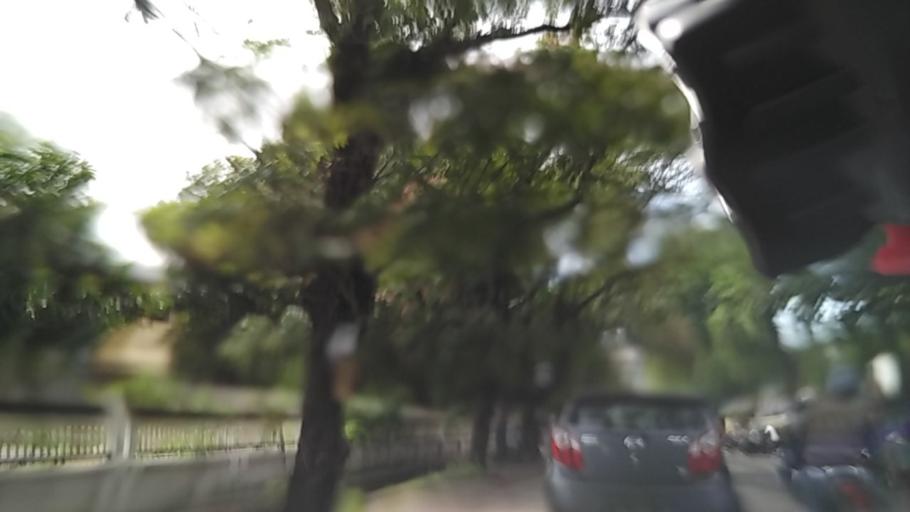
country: ID
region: Central Java
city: Semarang
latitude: -6.9968
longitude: 110.4273
